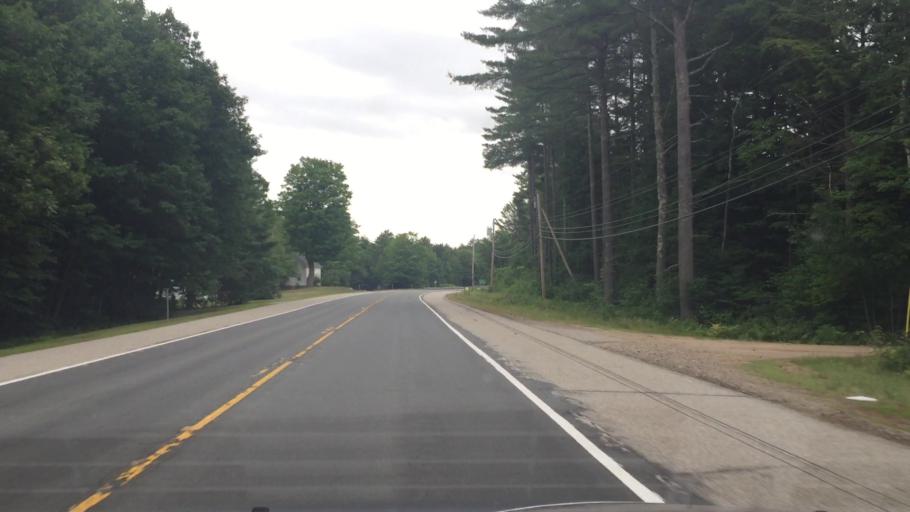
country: US
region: New Hampshire
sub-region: Carroll County
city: Tamworth
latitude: 43.8303
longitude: -71.2787
